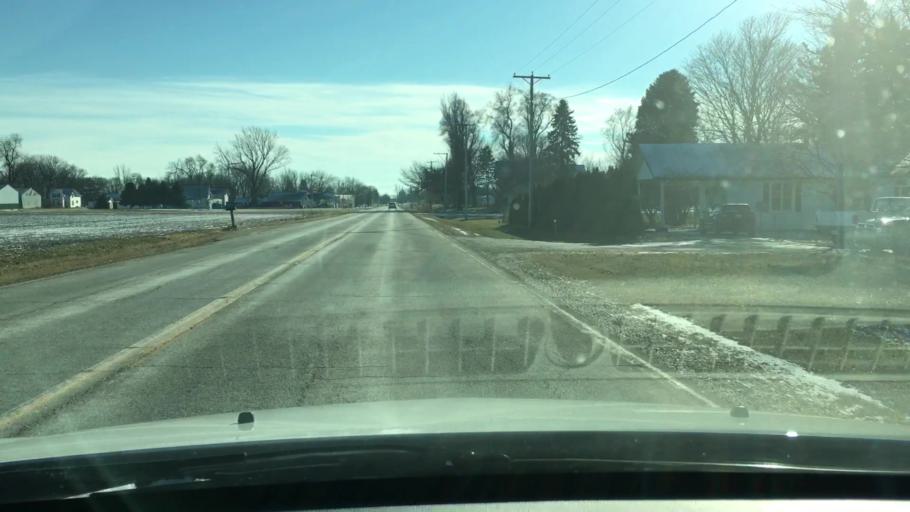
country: US
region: Illinois
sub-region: LaSalle County
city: Mendota
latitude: 41.6977
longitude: -89.0914
